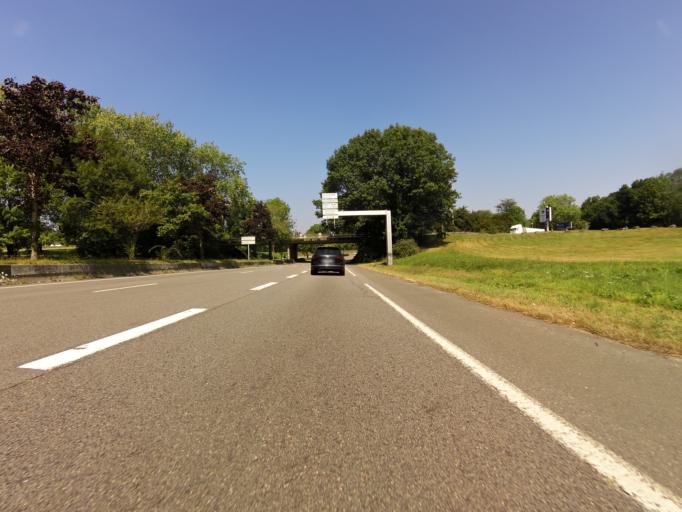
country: FR
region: Brittany
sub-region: Departement du Finistere
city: Quimper
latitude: 47.9840
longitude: -4.1115
